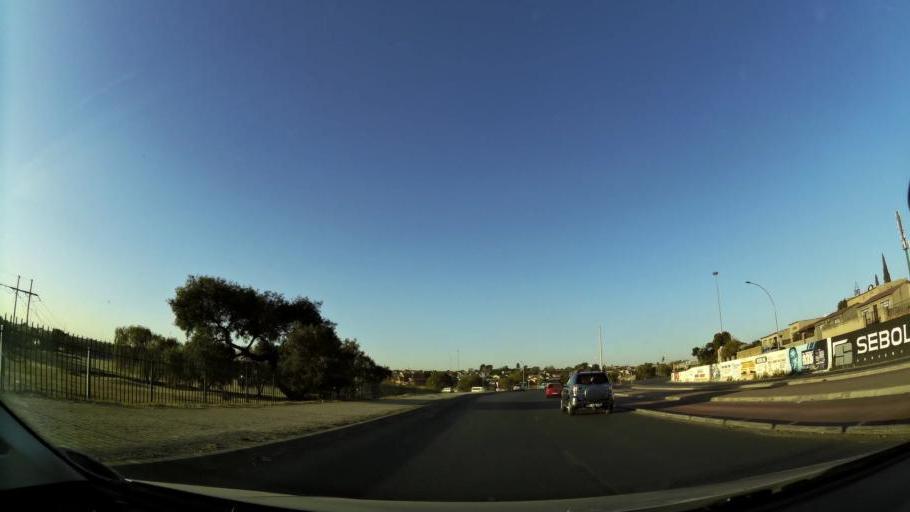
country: ZA
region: Gauteng
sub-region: Ekurhuleni Metropolitan Municipality
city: Tembisa
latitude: -26.0161
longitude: 28.2035
